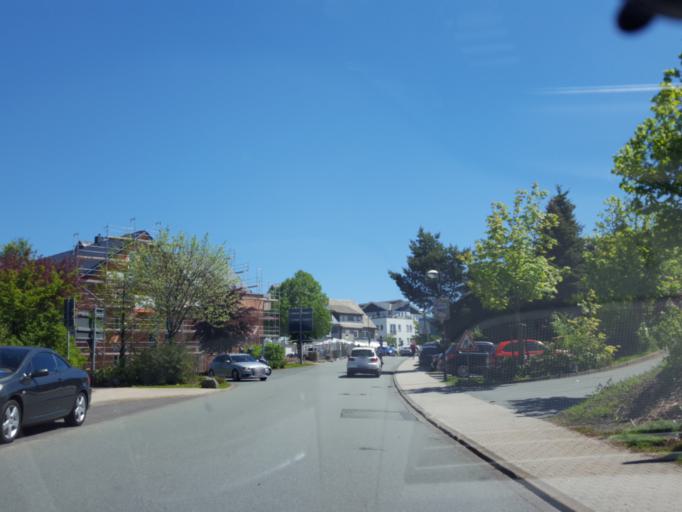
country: DE
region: North Rhine-Westphalia
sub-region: Regierungsbezirk Arnsberg
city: Winterberg
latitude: 51.1945
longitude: 8.5292
